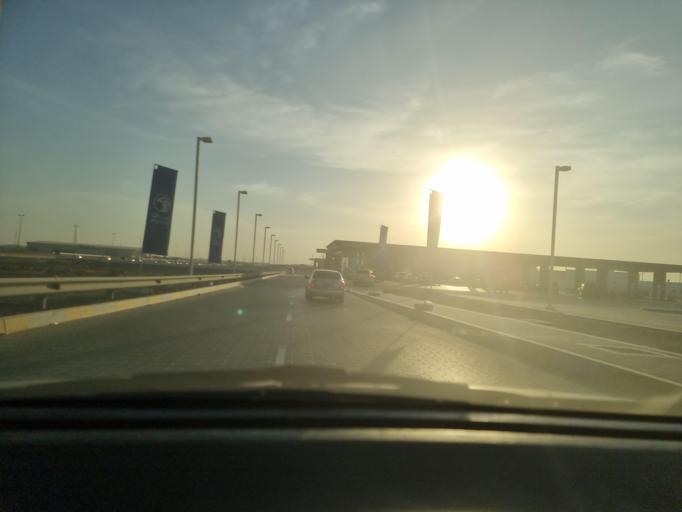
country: AE
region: Abu Dhabi
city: Abu Dhabi
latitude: 24.3167
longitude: 54.6786
